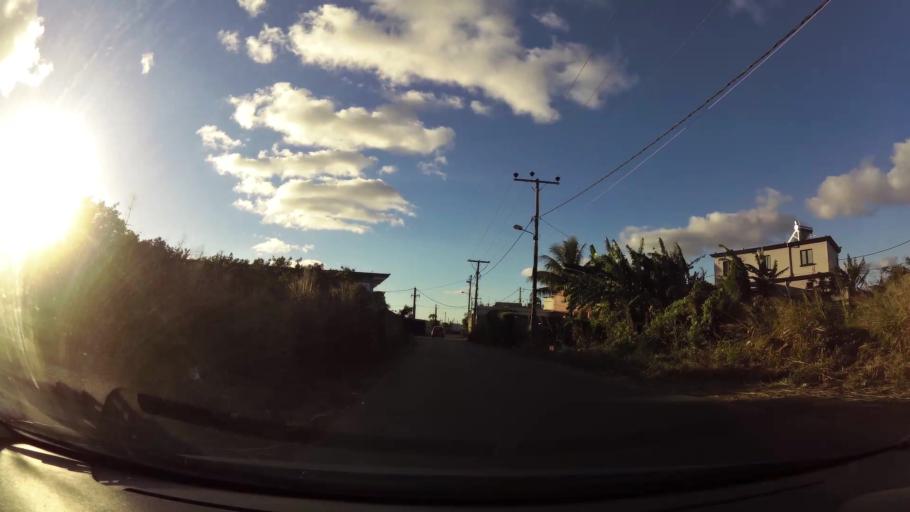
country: MU
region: Plaines Wilhems
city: Quatre Bornes
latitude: -20.2593
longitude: 57.4617
